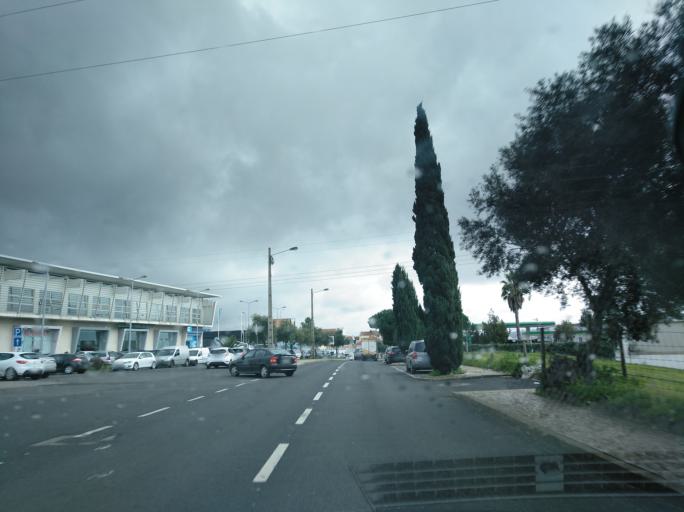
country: PT
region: Lisbon
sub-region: Odivelas
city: Famoes
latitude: 38.7865
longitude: -9.2089
